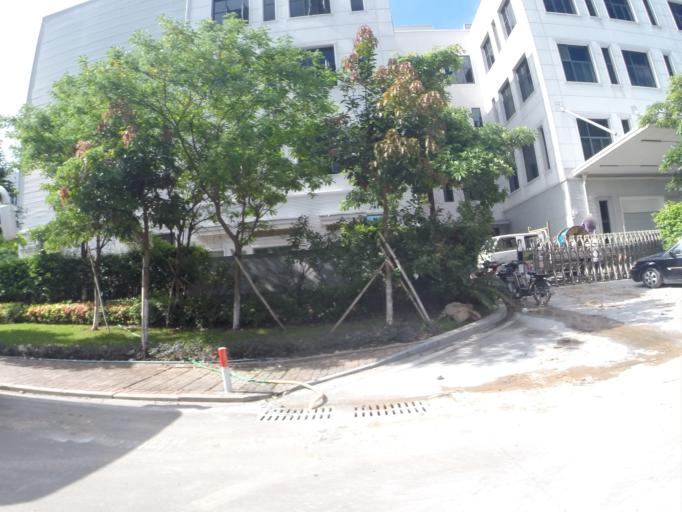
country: CN
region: Guangdong
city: Tangjiawan
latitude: 22.3928
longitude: 113.5537
